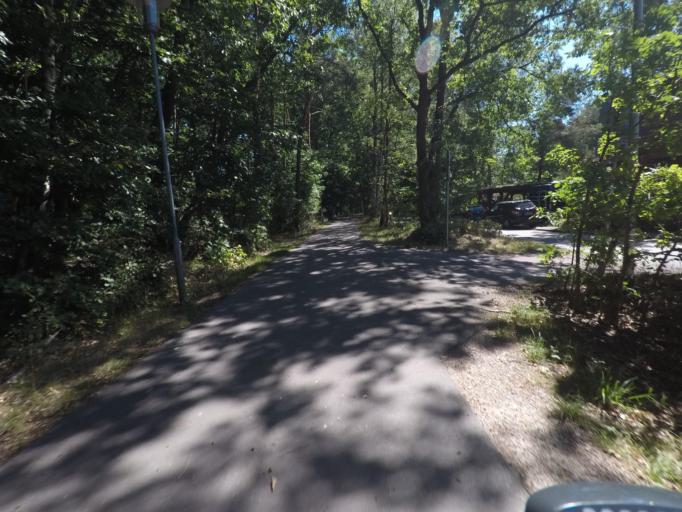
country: DE
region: Schleswig-Holstein
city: Lutjensee
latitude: 53.6405
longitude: 10.3710
